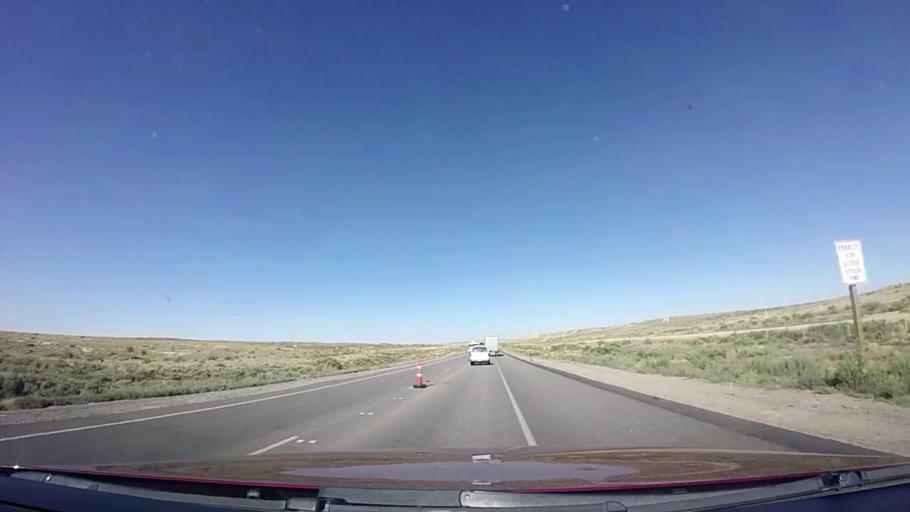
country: US
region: Wyoming
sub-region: Carbon County
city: Rawlins
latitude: 41.7059
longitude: -107.8530
